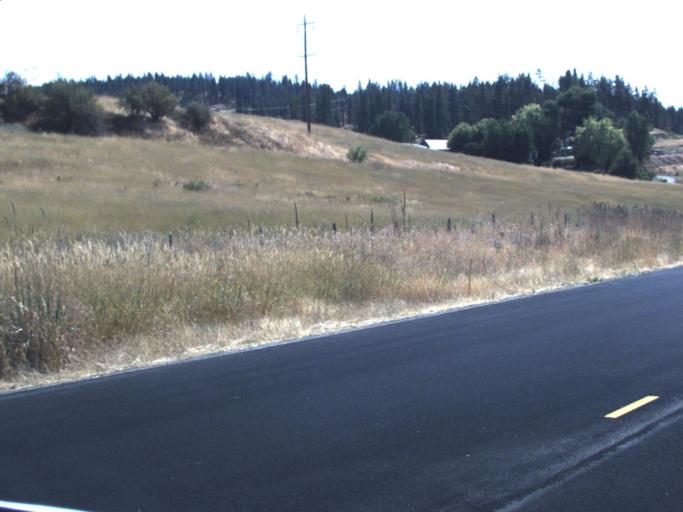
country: US
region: Washington
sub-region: Stevens County
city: Colville
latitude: 48.5046
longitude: -117.9022
